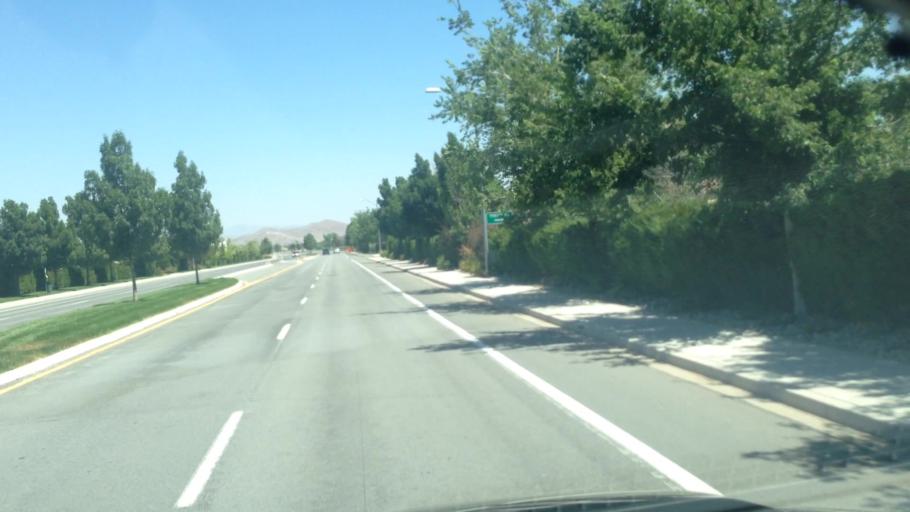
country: US
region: Nevada
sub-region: Washoe County
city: Sparks
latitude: 39.4084
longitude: -119.7336
